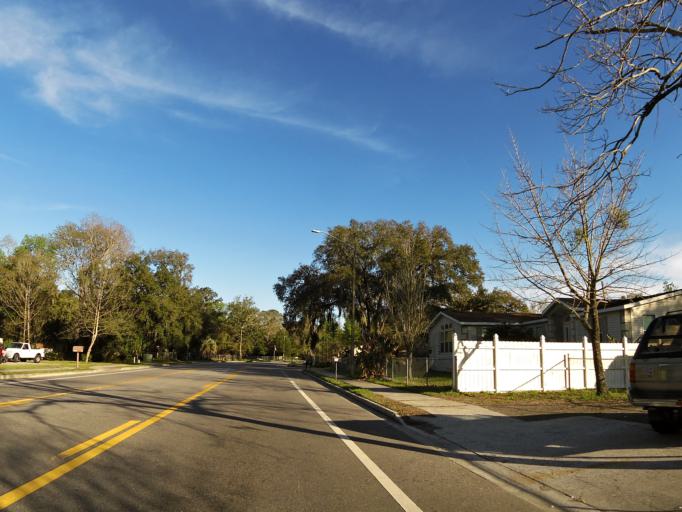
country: US
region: Florida
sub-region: Duval County
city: Jacksonville
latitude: 30.4607
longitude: -81.6158
